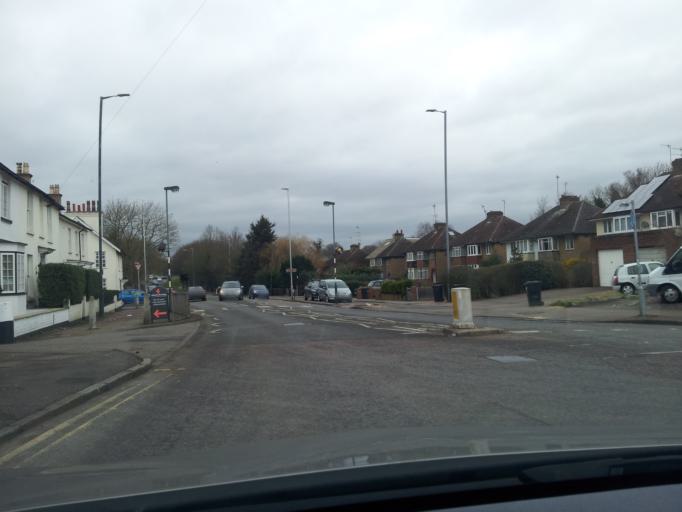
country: GB
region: England
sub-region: Hertfordshire
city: St Albans
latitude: 51.7564
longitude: -0.3492
